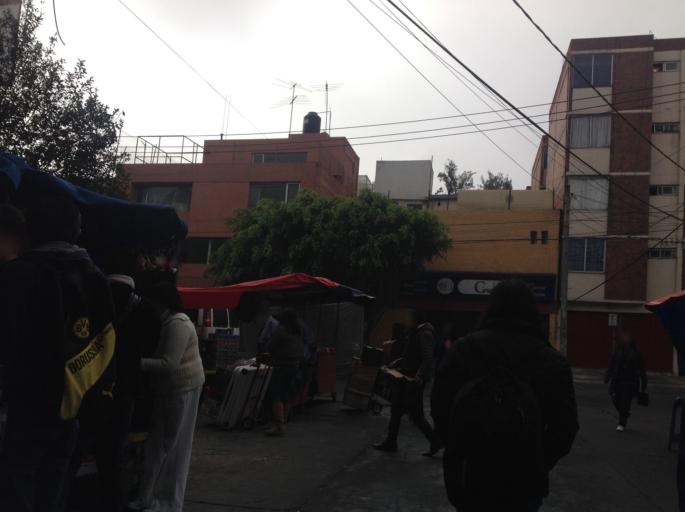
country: MX
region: Mexico City
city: Coyoacan
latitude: 19.3346
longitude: -99.1780
